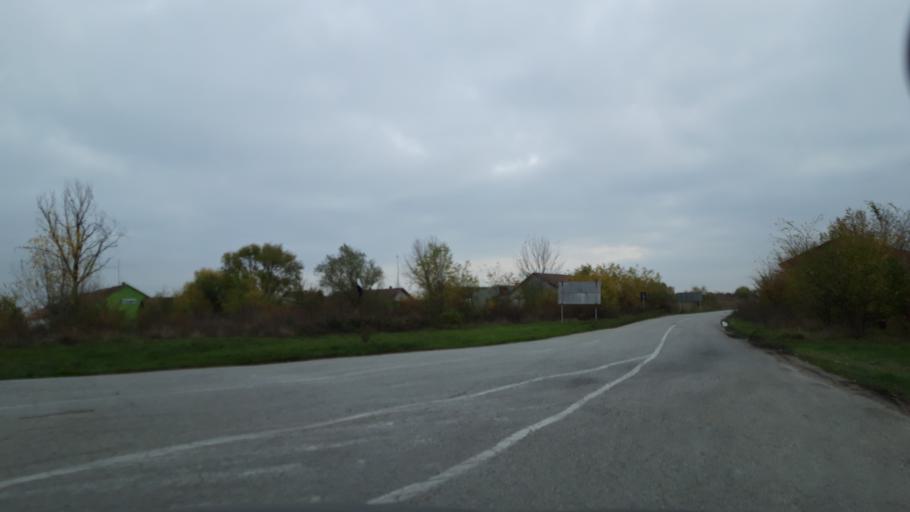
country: RS
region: Autonomna Pokrajina Vojvodina
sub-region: Severnobanatski Okrug
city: Novi Knezevac
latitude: 46.0503
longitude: 20.1035
